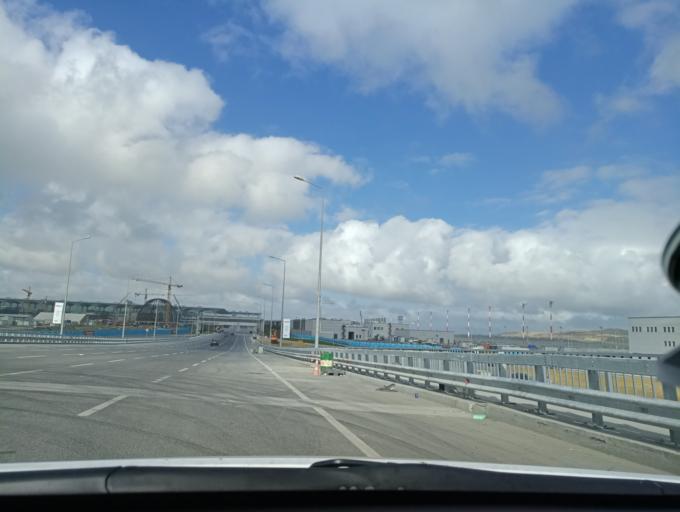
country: TR
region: Istanbul
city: Durusu
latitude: 41.2481
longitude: 28.7467
